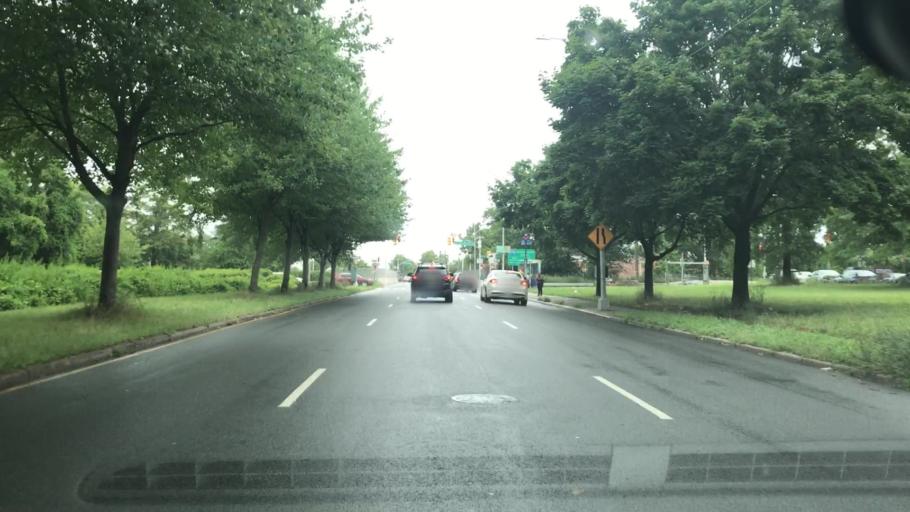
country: US
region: New Jersey
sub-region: Hudson County
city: Bayonne
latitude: 40.6046
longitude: -74.0768
